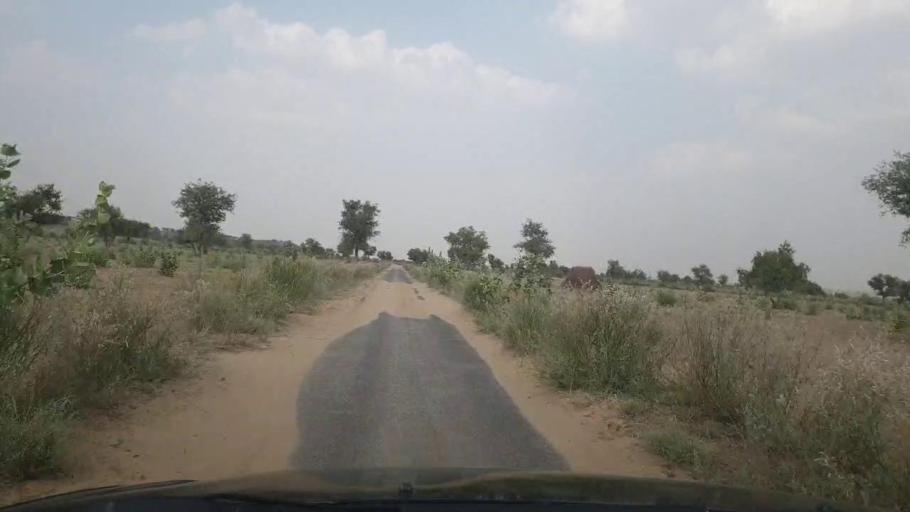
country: PK
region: Sindh
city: Islamkot
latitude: 24.9101
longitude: 70.5602
